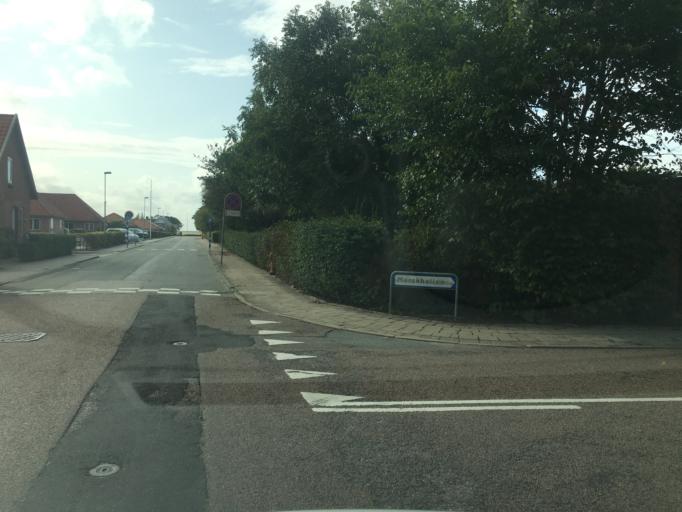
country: DE
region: Schleswig-Holstein
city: Klanxbull
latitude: 54.9652
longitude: 8.6909
